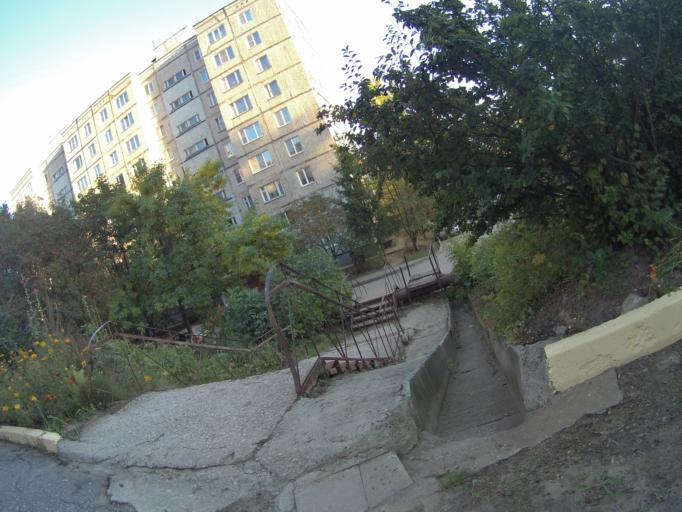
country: RU
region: Vladimir
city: Vladimir
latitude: 56.1087
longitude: 40.3537
